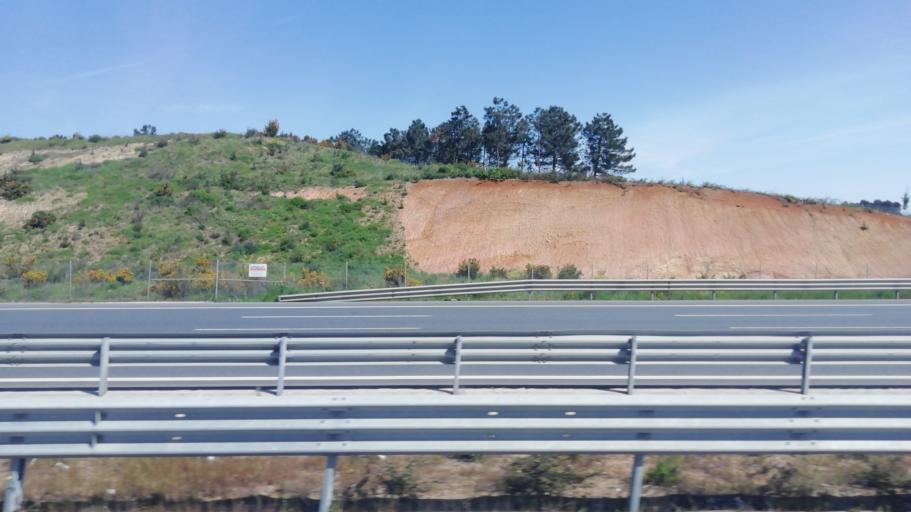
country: TR
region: Istanbul
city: Mahmut Sevket Pasa
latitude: 41.1986
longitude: 29.1502
